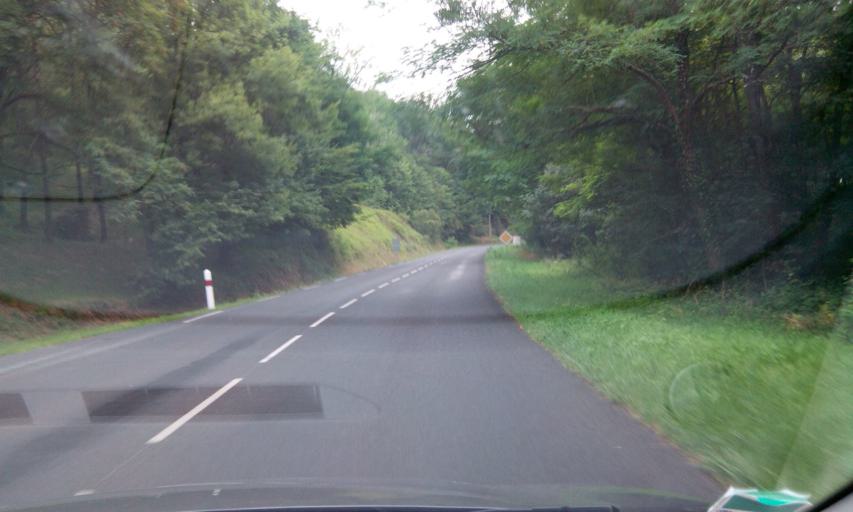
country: FR
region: Limousin
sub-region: Departement de la Correze
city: Meyssac
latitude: 45.0701
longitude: 1.6451
